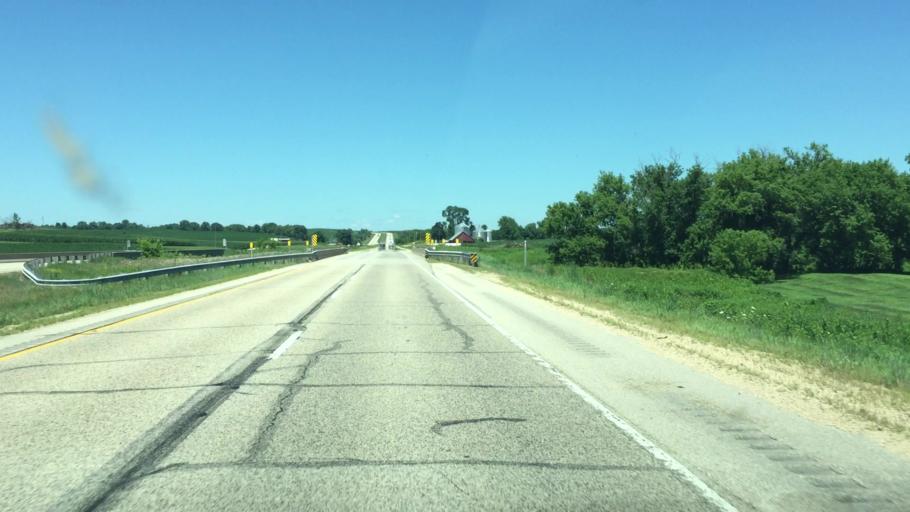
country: US
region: Iowa
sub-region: Jackson County
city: Maquoketa
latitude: 42.1723
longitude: -90.6738
